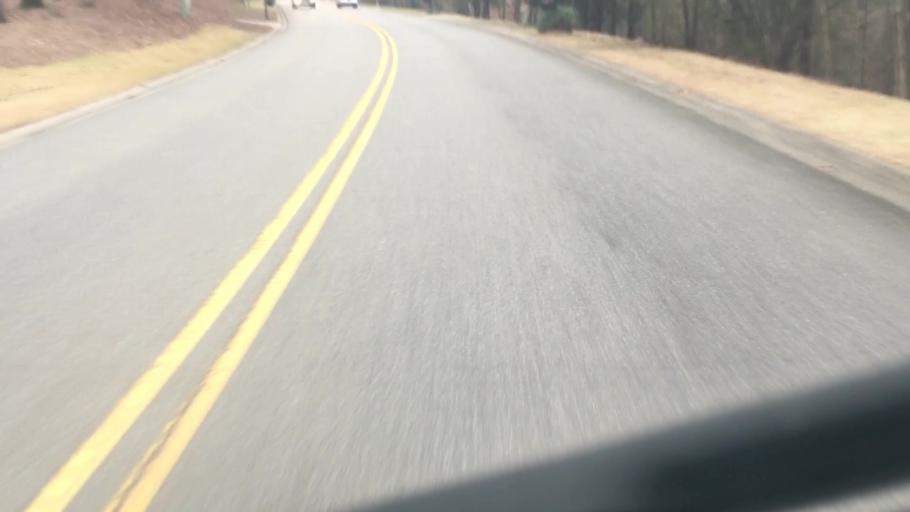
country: US
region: Alabama
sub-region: Jefferson County
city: Hoover
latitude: 33.3488
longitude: -86.8111
